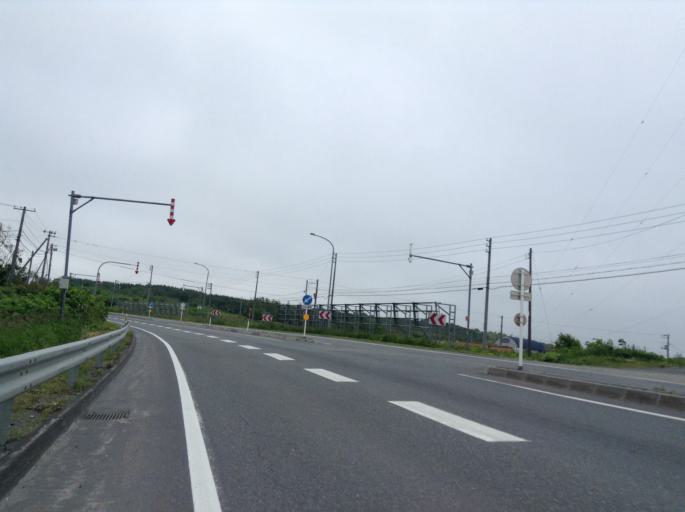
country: JP
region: Hokkaido
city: Wakkanai
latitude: 45.3763
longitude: 141.7122
